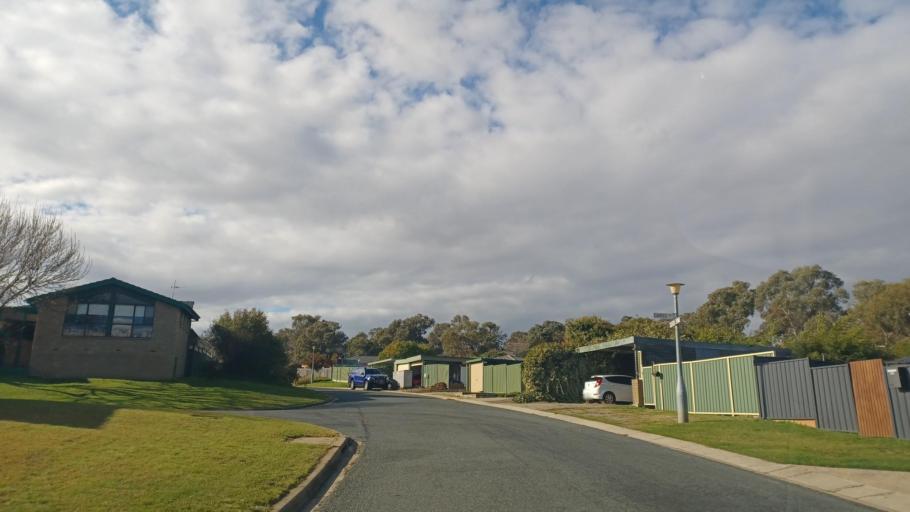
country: AU
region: Australian Capital Territory
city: Belconnen
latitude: -35.2017
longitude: 149.0415
